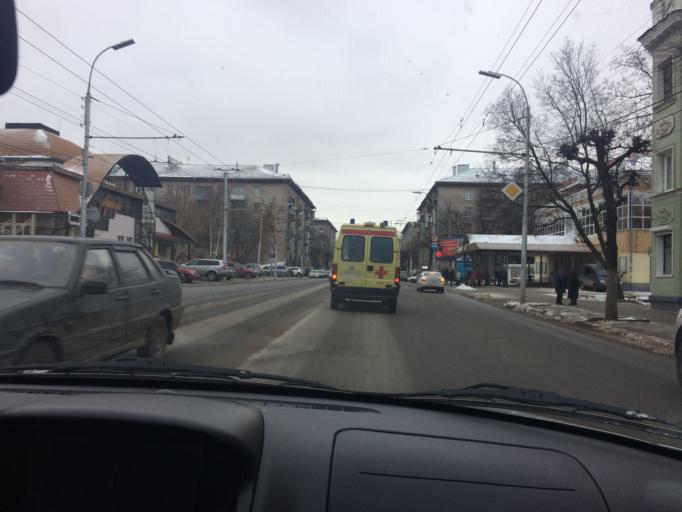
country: RU
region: Rjazan
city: Ryazan'
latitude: 54.6282
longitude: 39.7163
